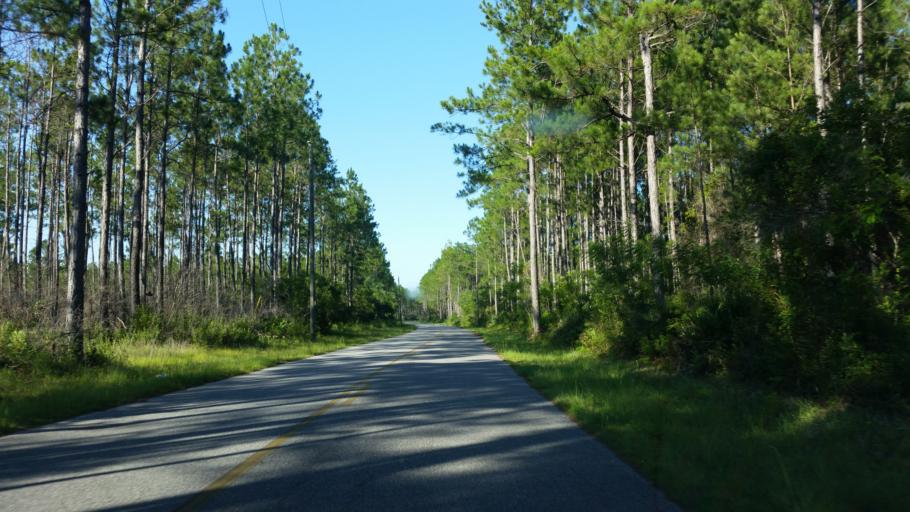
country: US
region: Florida
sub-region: Escambia County
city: Bellview
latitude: 30.4684
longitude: -87.4064
